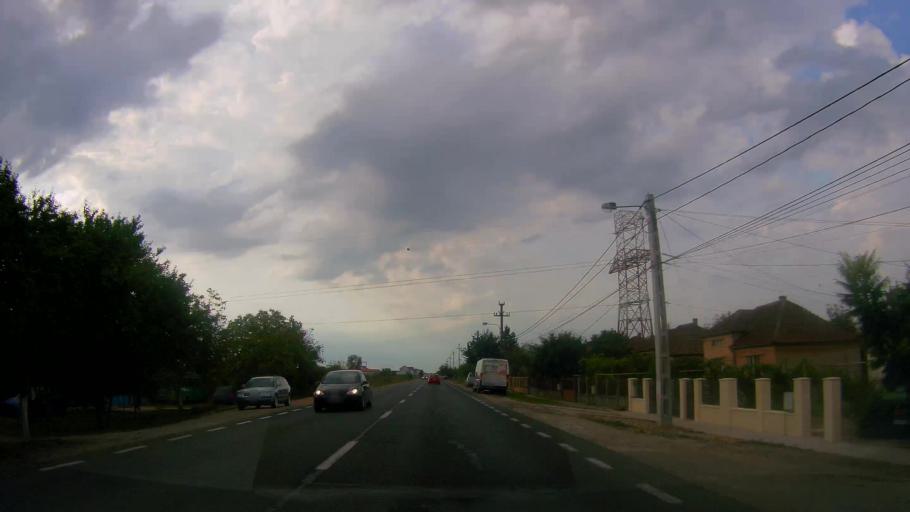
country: RO
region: Satu Mare
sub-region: Municipiul Satu Mare
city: Satu Mare
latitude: 47.7606
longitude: 22.8833
